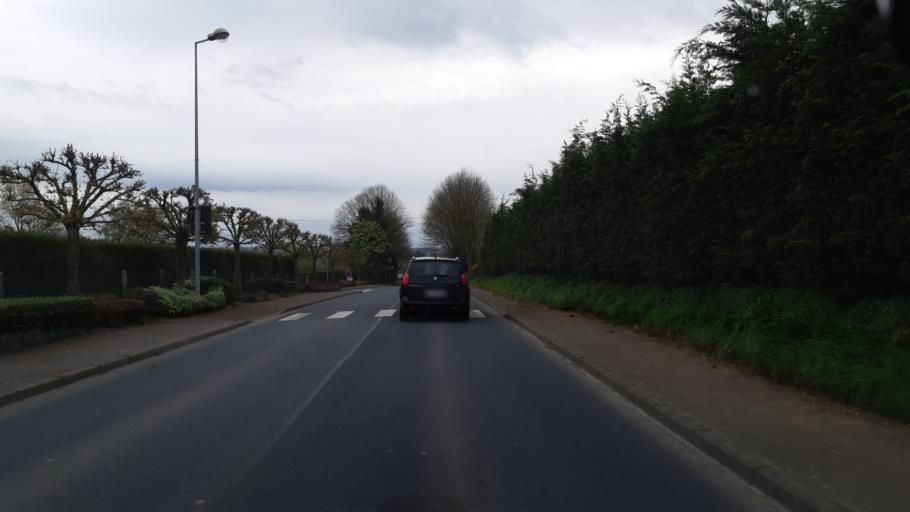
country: FR
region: Lower Normandy
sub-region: Departement de la Manche
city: Tessy-sur-Vire
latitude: 49.0271
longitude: -1.1448
